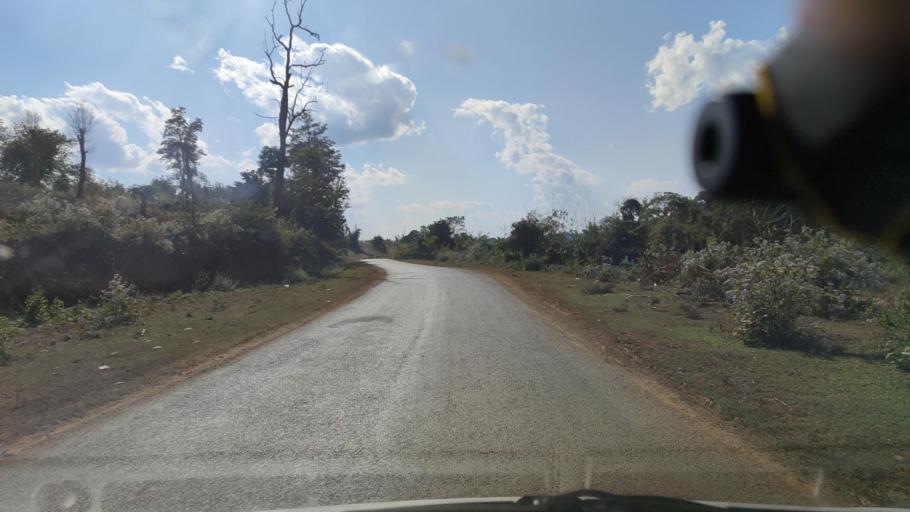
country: MM
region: Shan
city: Lashio
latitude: 22.1200
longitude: 98.0373
